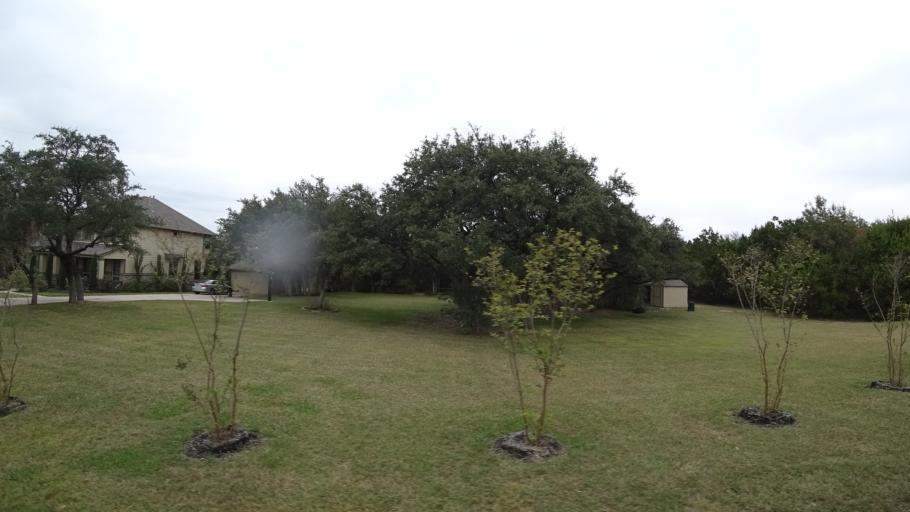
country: US
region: Texas
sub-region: Williamson County
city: Anderson Mill
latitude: 30.4471
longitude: -97.8367
